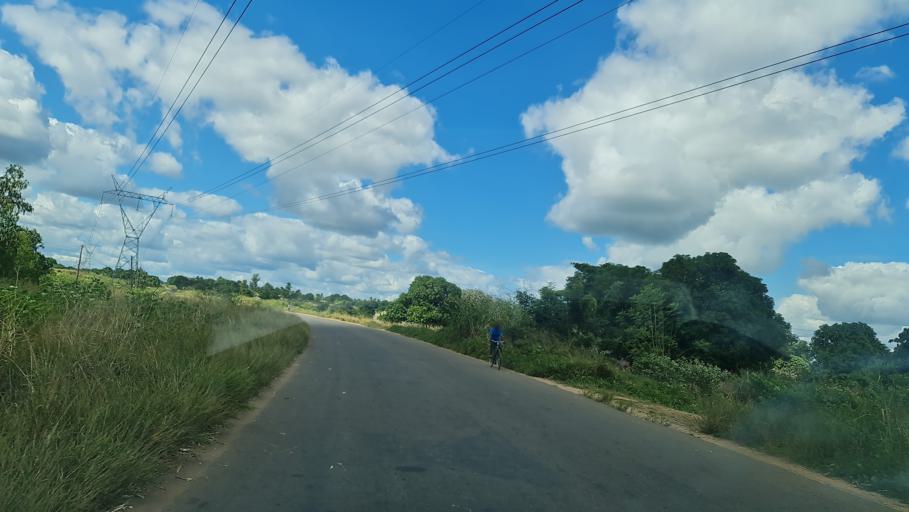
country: MZ
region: Zambezia
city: Quelimane
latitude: -17.5246
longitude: 36.2688
